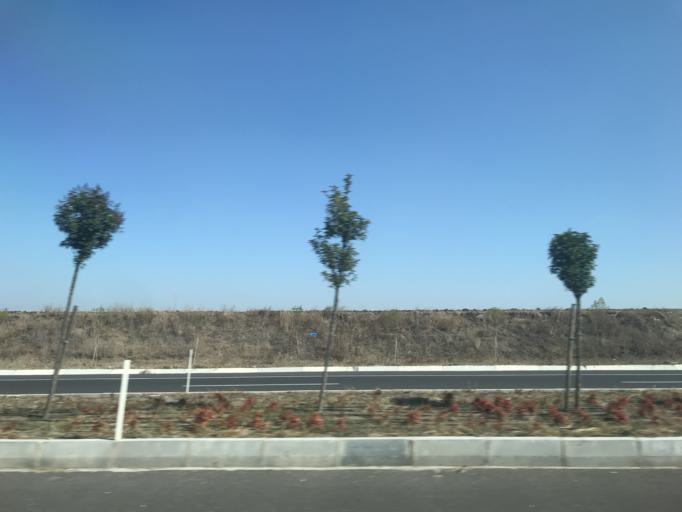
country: TR
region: Tekirdag
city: Muratli
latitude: 41.1980
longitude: 27.5379
